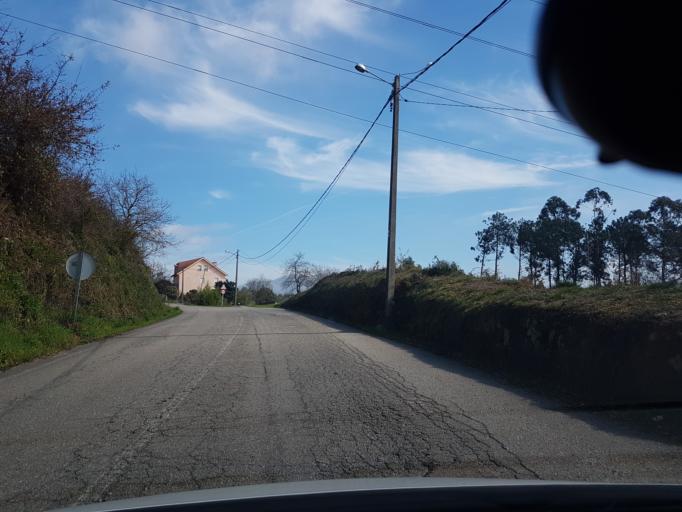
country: ES
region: Galicia
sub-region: Provincia de Pontevedra
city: Porrino
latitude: 42.2142
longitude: -8.6406
